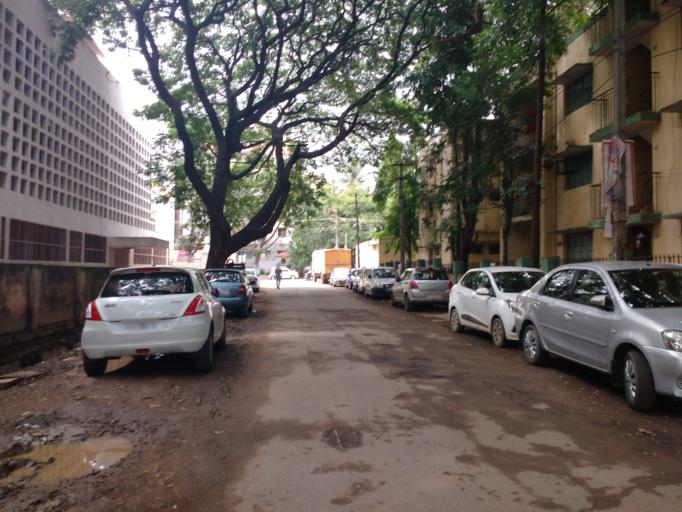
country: IN
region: Karnataka
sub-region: Bangalore Urban
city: Bangalore
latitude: 12.9720
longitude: 77.6386
